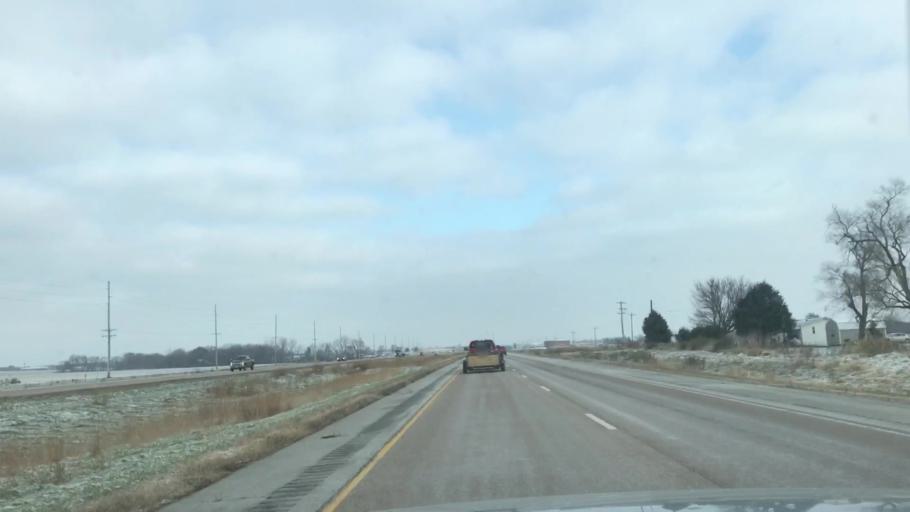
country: US
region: Illinois
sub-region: Macoupin County
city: Staunton
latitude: 39.0048
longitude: -89.7496
